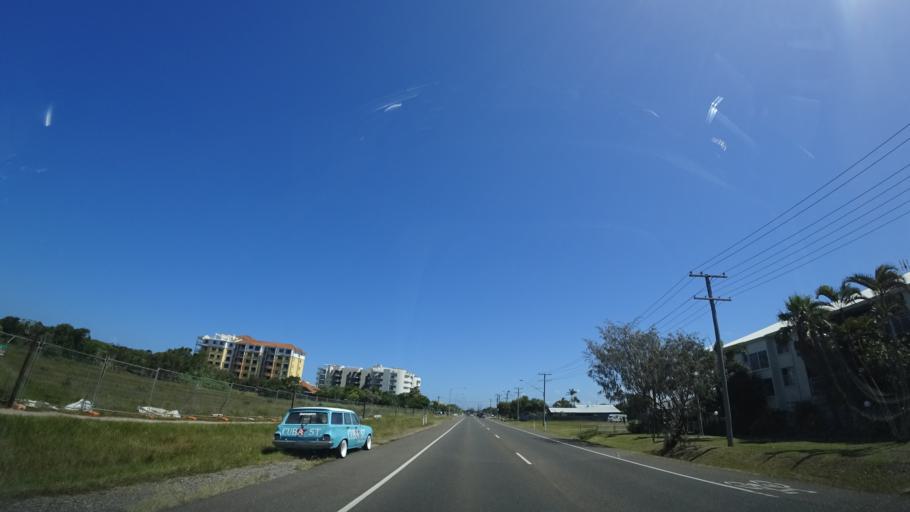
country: AU
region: Queensland
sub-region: Sunshine Coast
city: Coolum Beach
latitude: -26.5984
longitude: 153.0956
